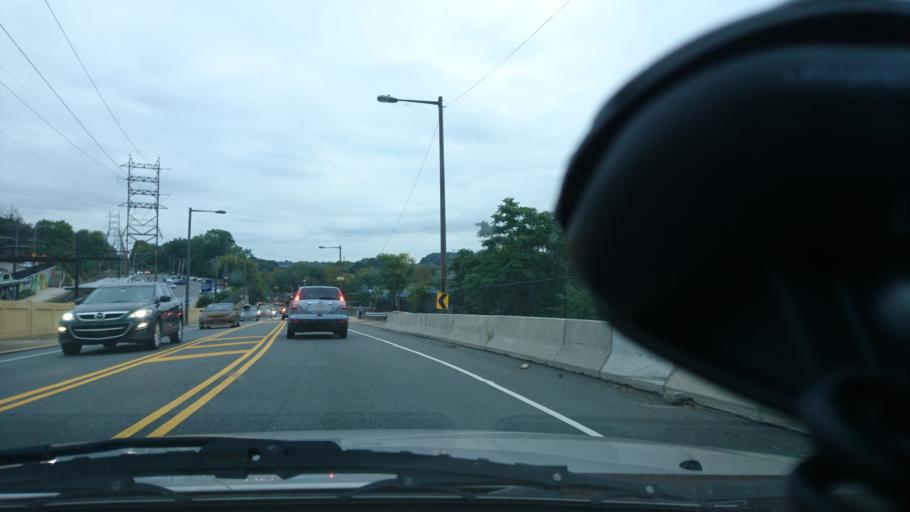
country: US
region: Pennsylvania
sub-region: Montgomery County
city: Bala-Cynwyd
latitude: 40.0168
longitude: -75.2112
